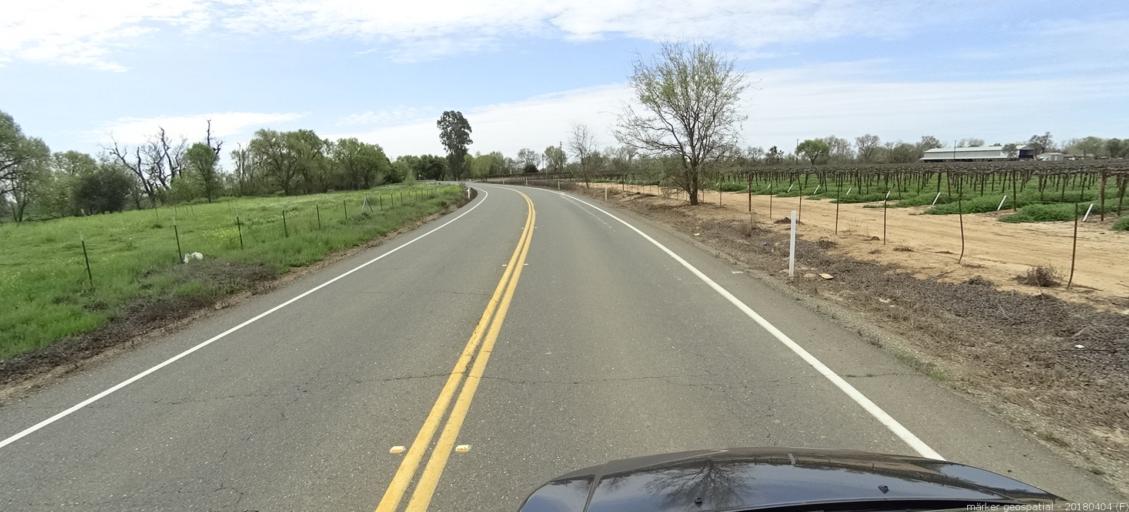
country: US
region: California
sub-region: Sacramento County
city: Clay
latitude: 38.2581
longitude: -121.1720
